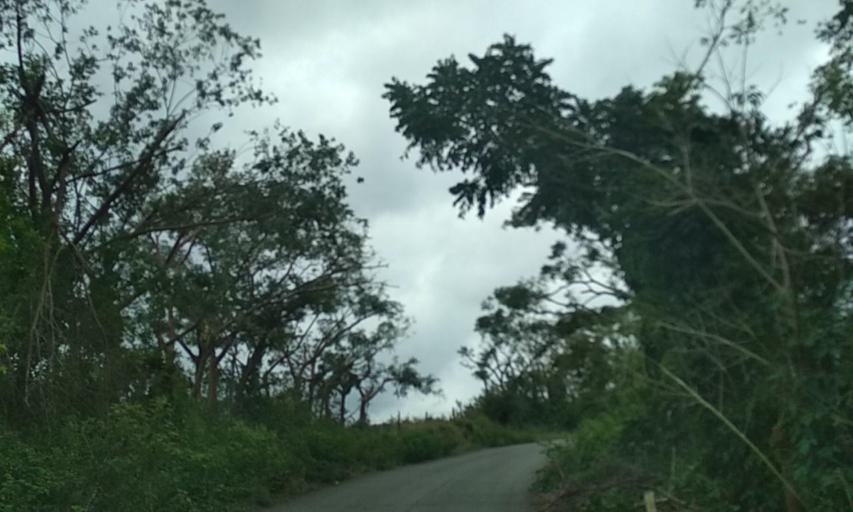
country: MX
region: Veracruz
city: Papantla de Olarte
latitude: 20.4754
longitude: -97.3093
